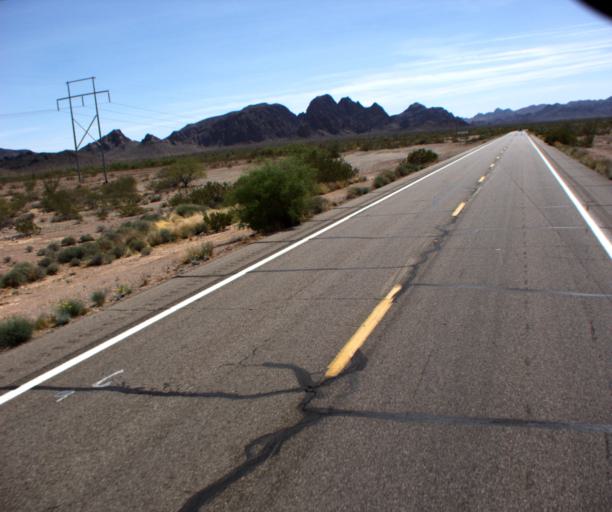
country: US
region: Arizona
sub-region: La Paz County
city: Quartzsite
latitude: 33.3131
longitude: -114.2169
